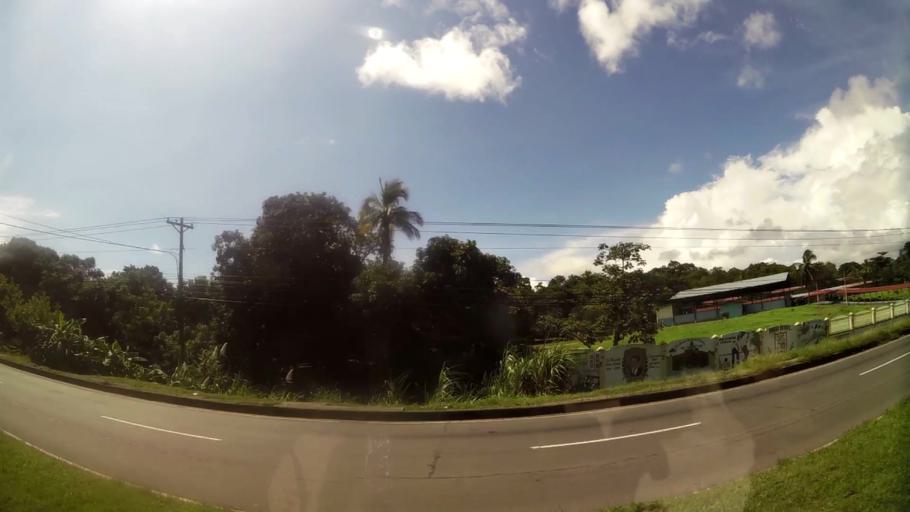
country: PA
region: Panama
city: Chame
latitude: 8.5812
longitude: -79.8843
